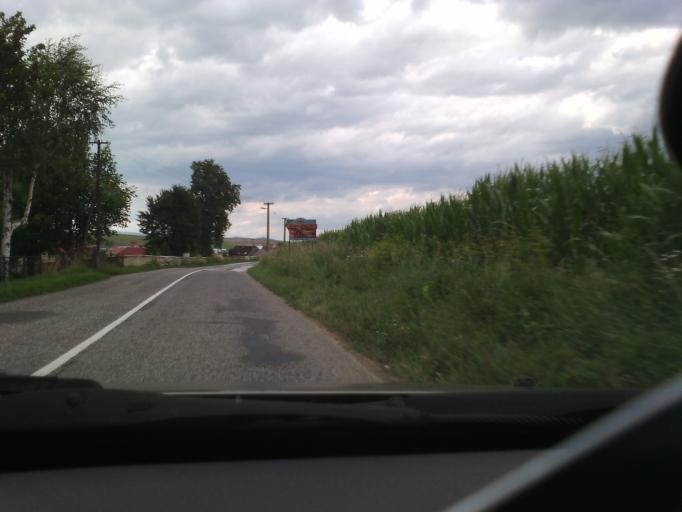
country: SK
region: Presovsky
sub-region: Okres Presov
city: Kezmarok
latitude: 49.1109
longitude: 20.3778
